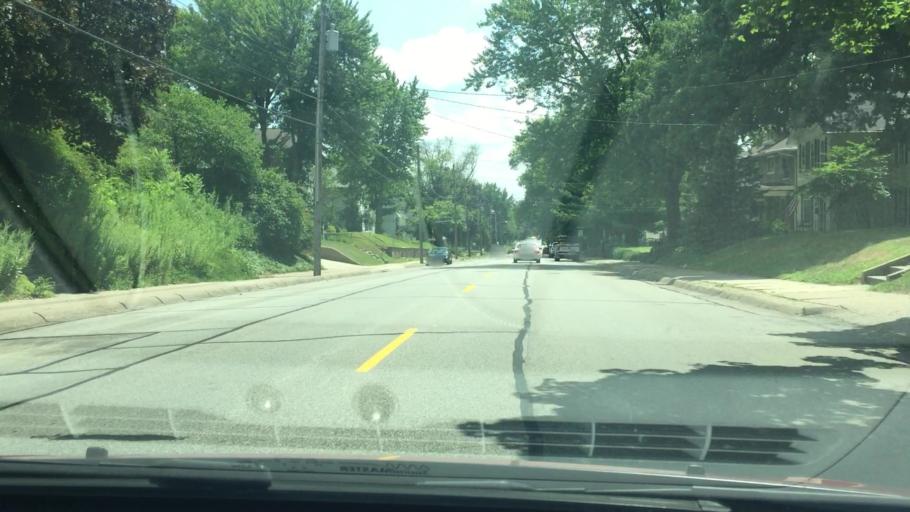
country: US
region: Iowa
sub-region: Muscatine County
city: Muscatine
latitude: 41.4323
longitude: -91.0505
